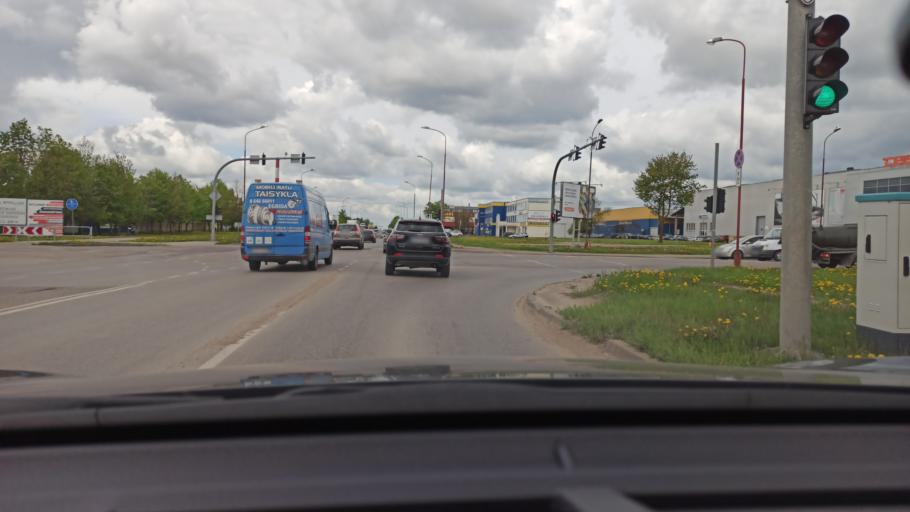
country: LT
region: Siauliu apskritis
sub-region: Siauliai
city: Siauliai
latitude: 55.9054
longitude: 23.3281
